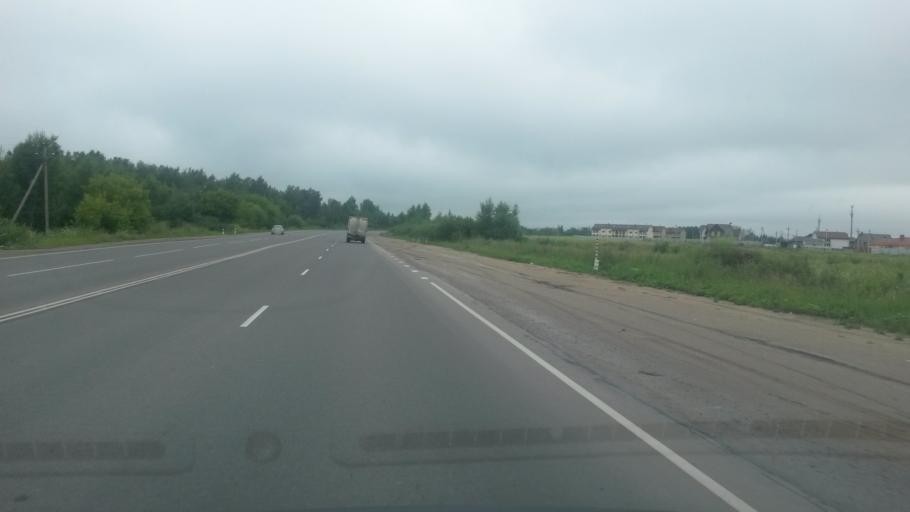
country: RU
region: Ivanovo
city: Novo-Talitsy
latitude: 57.0168
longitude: 40.8872
